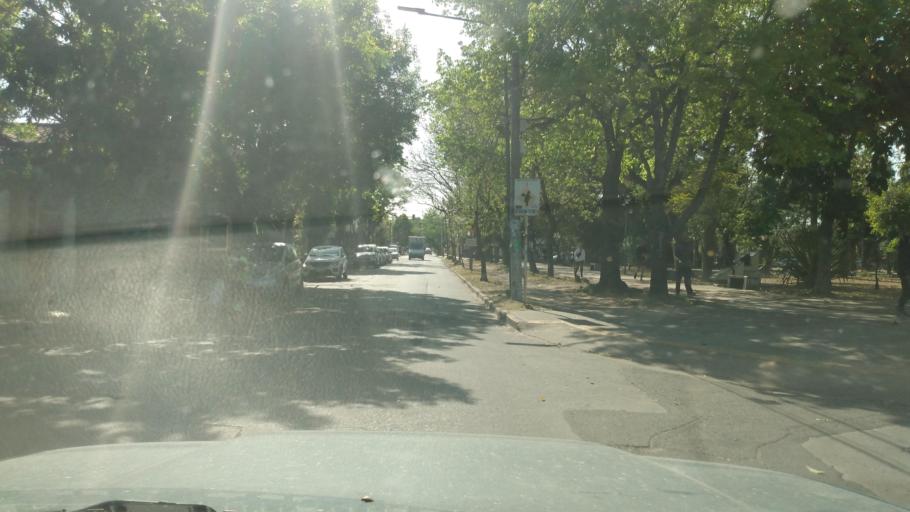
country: AR
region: Buenos Aires
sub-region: Partido de Moron
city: Moron
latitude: -34.6461
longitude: -58.5869
